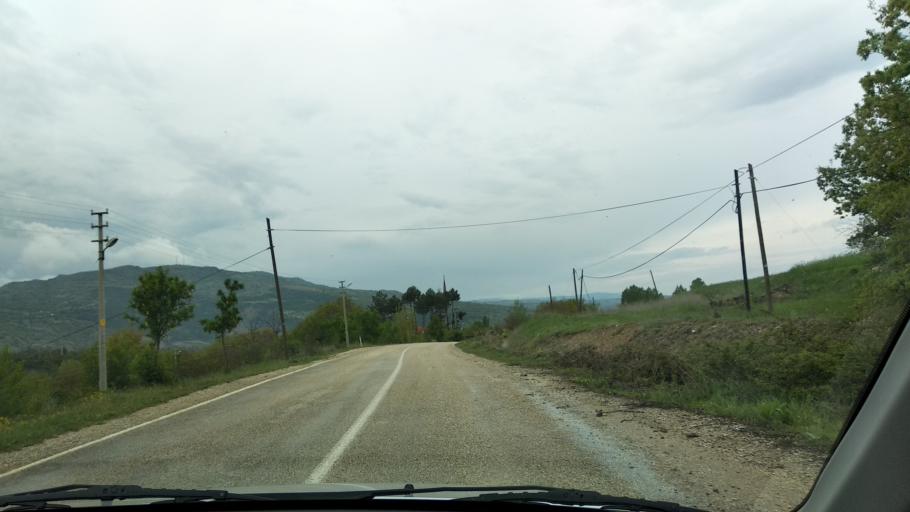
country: TR
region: Bolu
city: Seben
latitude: 40.4207
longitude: 31.5845
